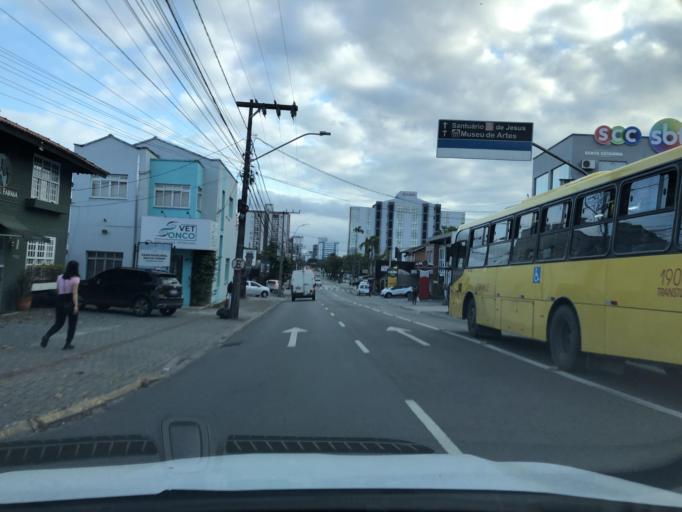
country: BR
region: Santa Catarina
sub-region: Joinville
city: Joinville
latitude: -26.2897
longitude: -48.8498
